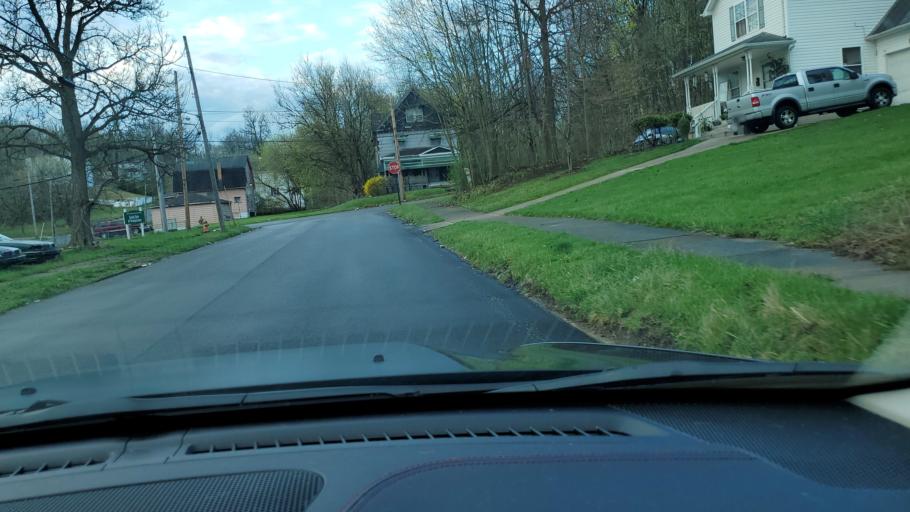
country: US
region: Ohio
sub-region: Mahoning County
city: Youngstown
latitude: 41.0977
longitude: -80.6670
